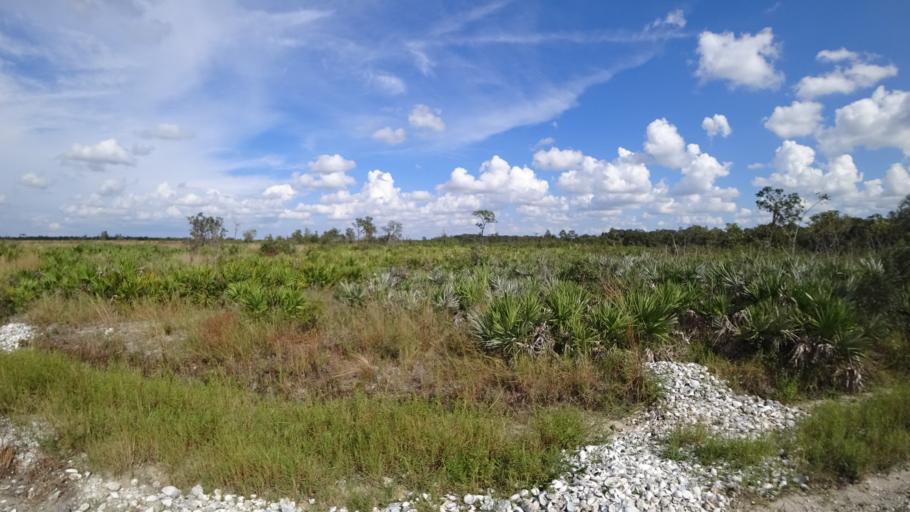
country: US
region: Florida
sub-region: Hillsborough County
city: Wimauma
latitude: 27.5245
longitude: -82.1273
